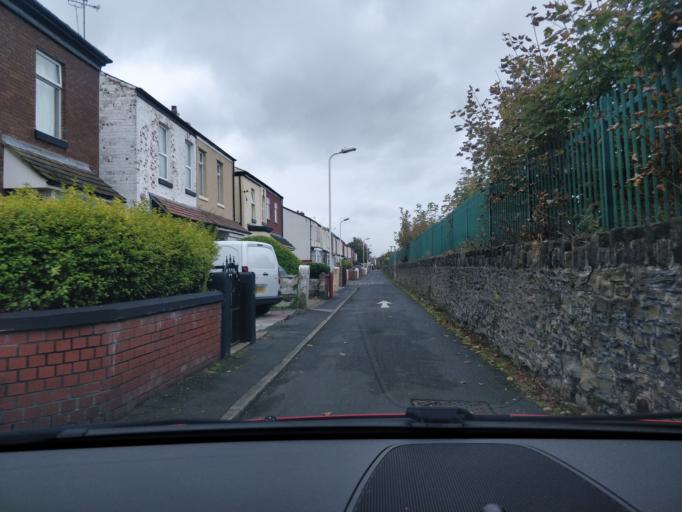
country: GB
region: England
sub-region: Sefton
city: Southport
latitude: 53.6409
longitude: -3.0045
